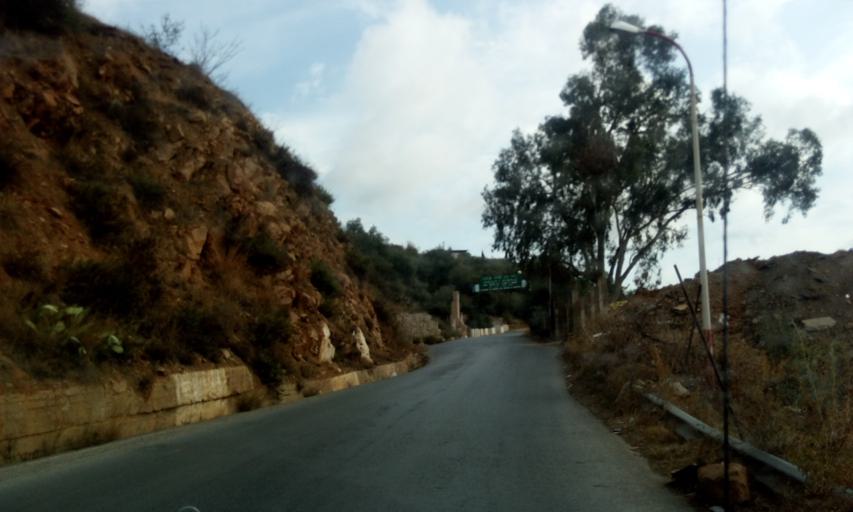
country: DZ
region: Tizi Ouzou
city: Chemini
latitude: 36.6208
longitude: 4.6625
